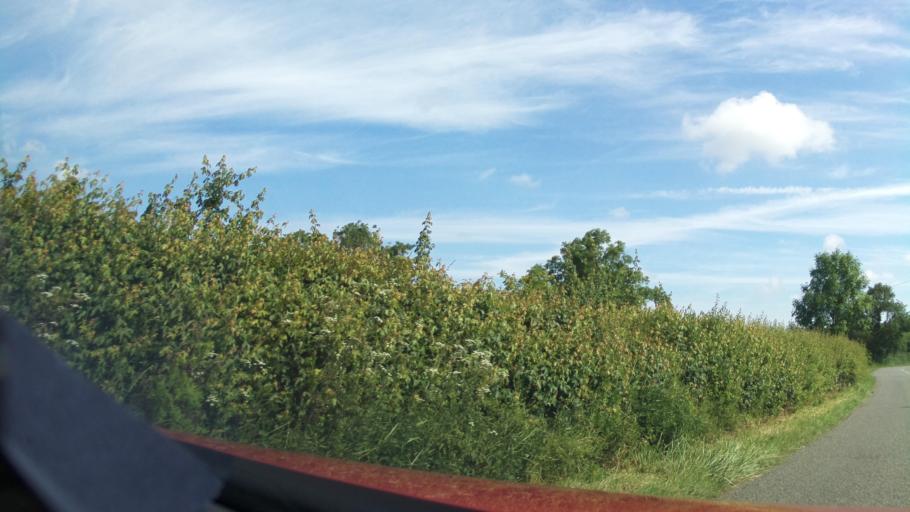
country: GB
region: England
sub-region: Lincolnshire
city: Skellingthorpe
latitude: 53.1490
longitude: -0.6316
